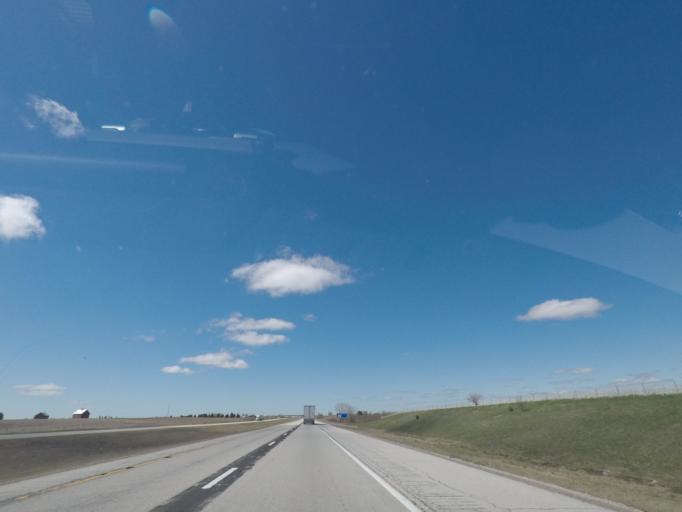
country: US
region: Illinois
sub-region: Livingston County
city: Odell
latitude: 41.0236
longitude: -88.5134
